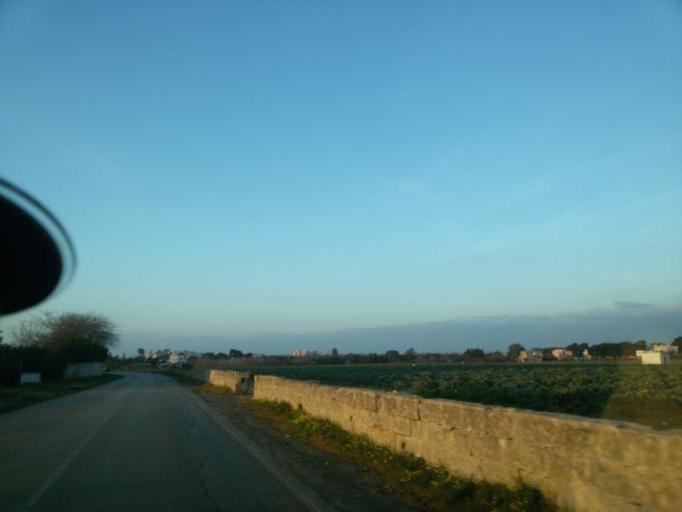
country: IT
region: Apulia
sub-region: Provincia di Brindisi
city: La Rosa
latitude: 40.6034
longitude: 17.9461
